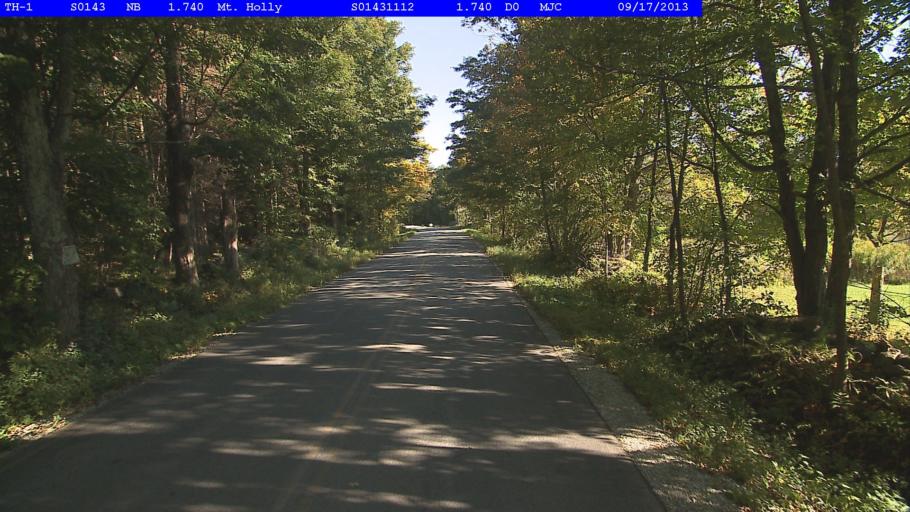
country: US
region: Vermont
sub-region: Rutland County
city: Rutland
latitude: 43.4241
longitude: -72.8196
